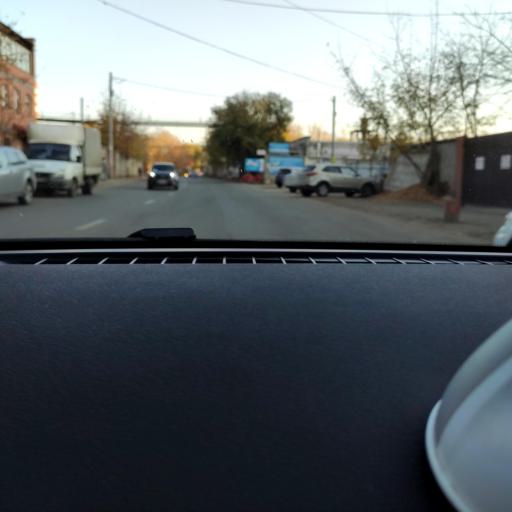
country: RU
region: Samara
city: Samara
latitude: 53.2192
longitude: 50.1953
